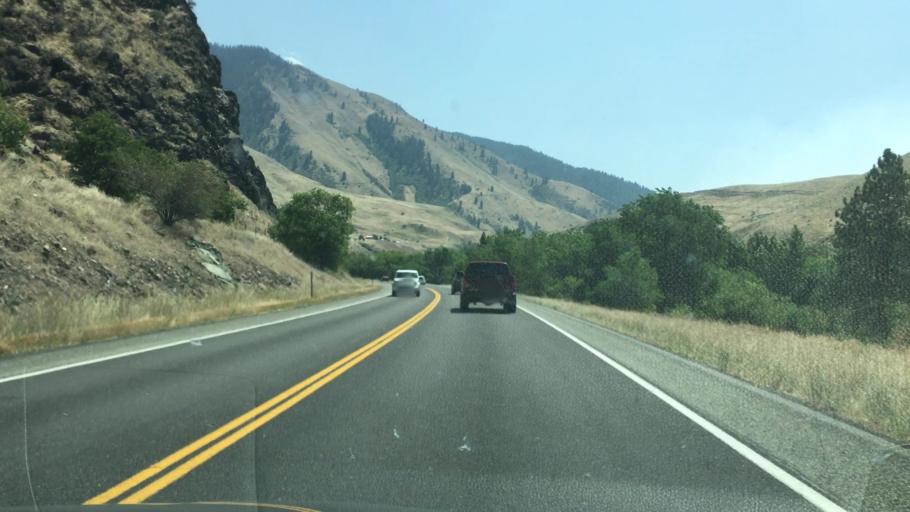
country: US
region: Idaho
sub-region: Valley County
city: McCall
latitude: 45.3483
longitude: -116.3554
